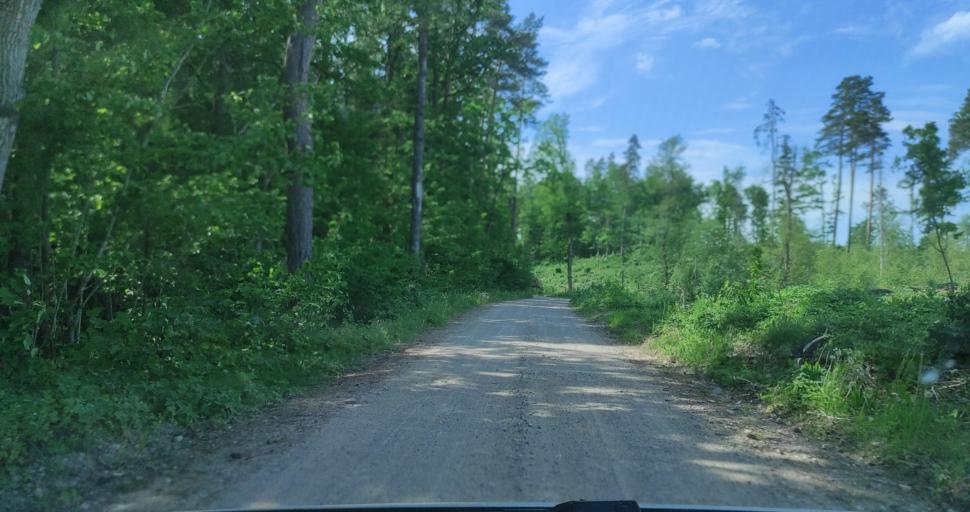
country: LV
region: Kuldigas Rajons
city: Kuldiga
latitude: 56.8498
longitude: 21.9191
